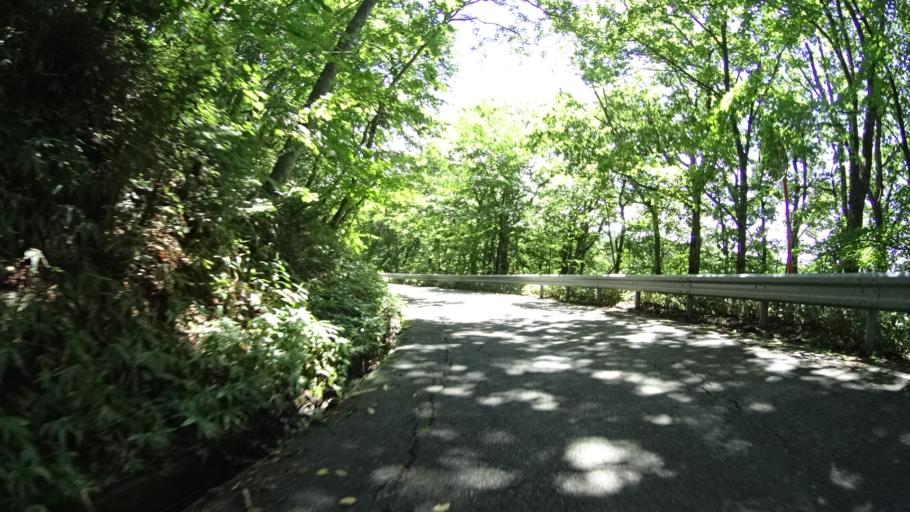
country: JP
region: Yamanashi
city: Enzan
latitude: 35.7340
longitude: 138.8315
